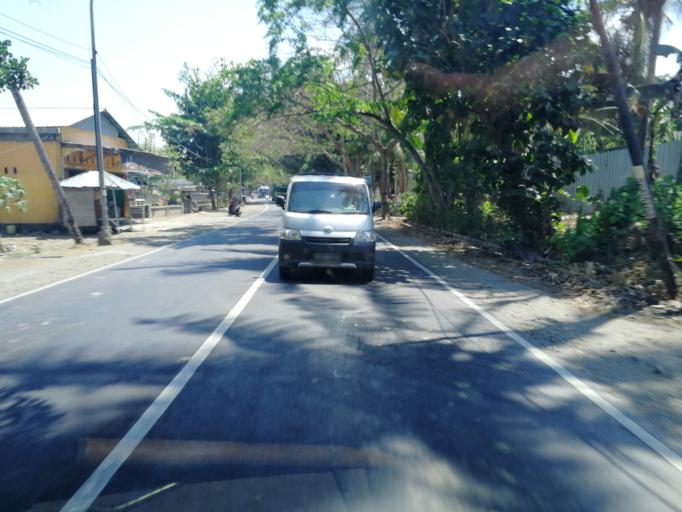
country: ID
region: West Nusa Tenggara
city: Jelateng Timur
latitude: -8.6961
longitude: 116.1067
